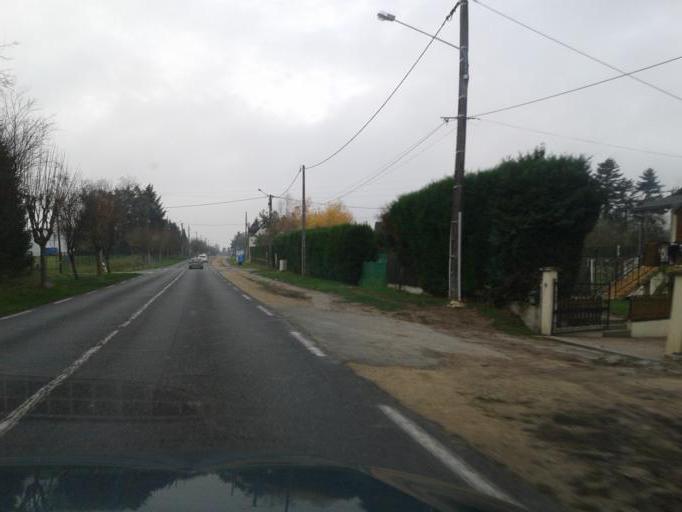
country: FR
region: Centre
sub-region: Departement du Loiret
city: Lailly-en-Val
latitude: 47.7780
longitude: 1.7010
